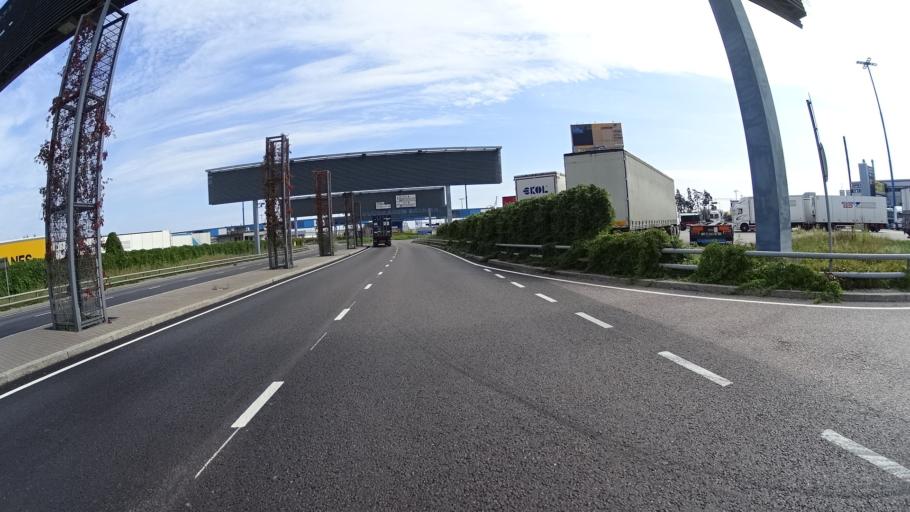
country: FI
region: Uusimaa
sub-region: Helsinki
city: Vantaa
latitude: 60.2246
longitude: 25.1717
